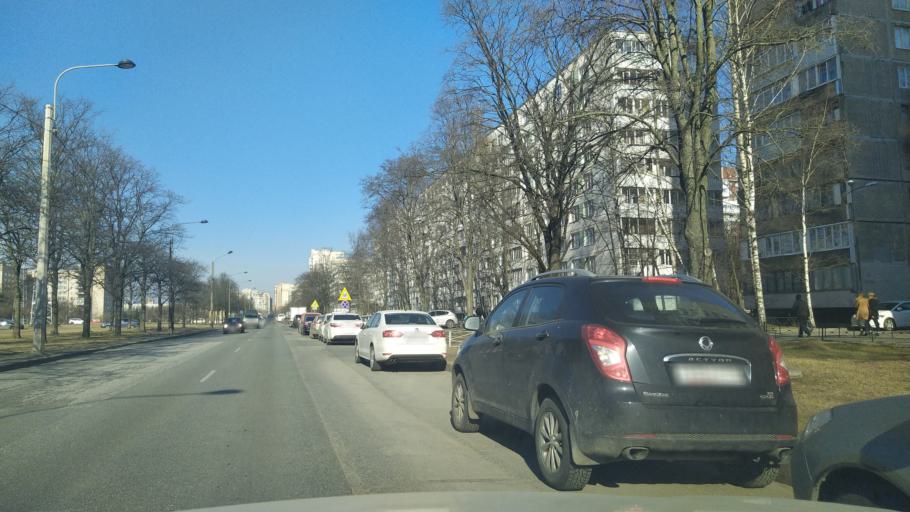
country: RU
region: Leningrad
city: Akademicheskoe
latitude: 60.0200
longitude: 30.3897
